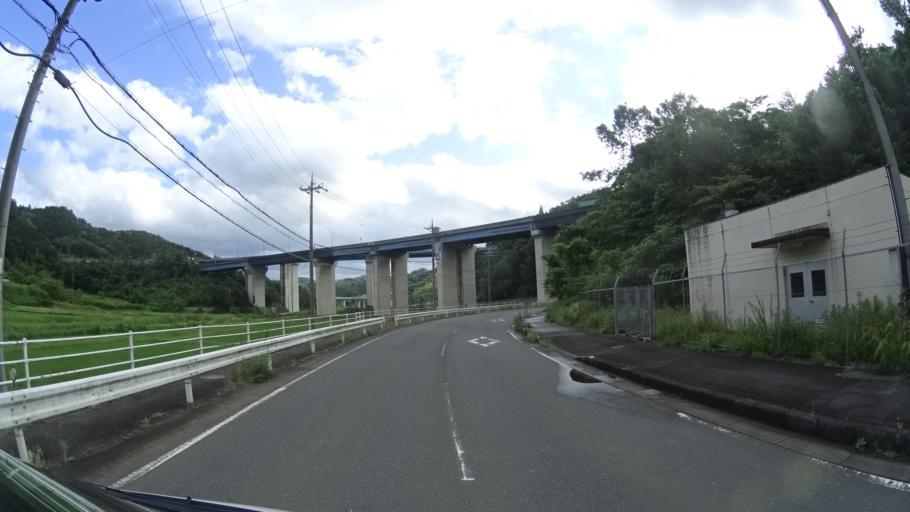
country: JP
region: Kyoto
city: Ayabe
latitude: 35.3534
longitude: 135.2920
